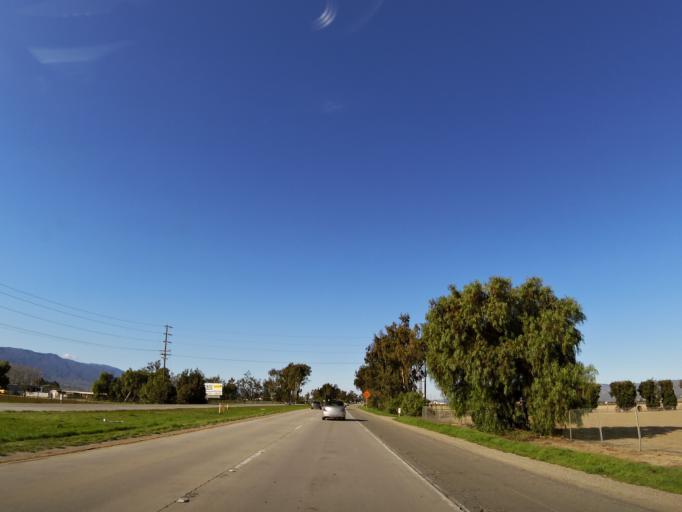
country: US
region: California
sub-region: Monterey County
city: Greenfield
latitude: 36.3339
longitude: -121.2491
